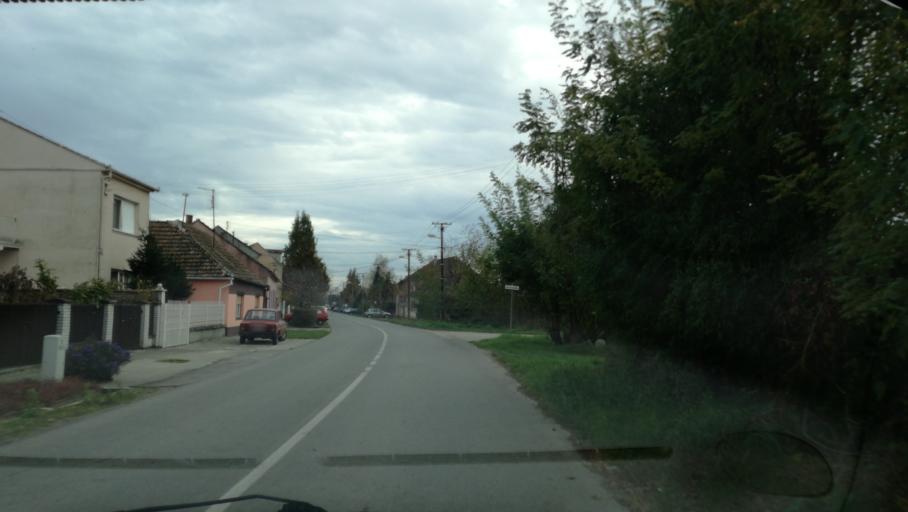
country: RS
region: Autonomna Pokrajina Vojvodina
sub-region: Severnobanatski Okrug
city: Kikinda
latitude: 45.8420
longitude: 20.4686
